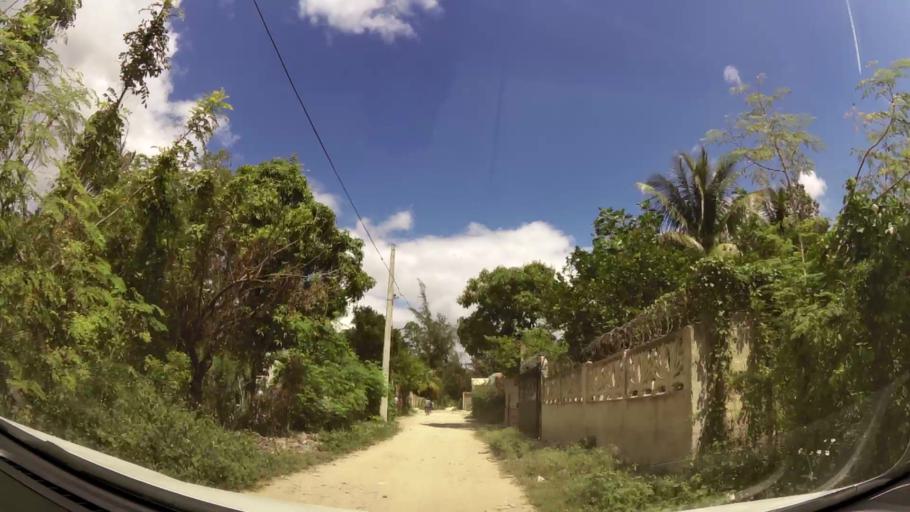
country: DO
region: Santo Domingo
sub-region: Santo Domingo
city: Boca Chica
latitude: 18.4524
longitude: -69.6507
